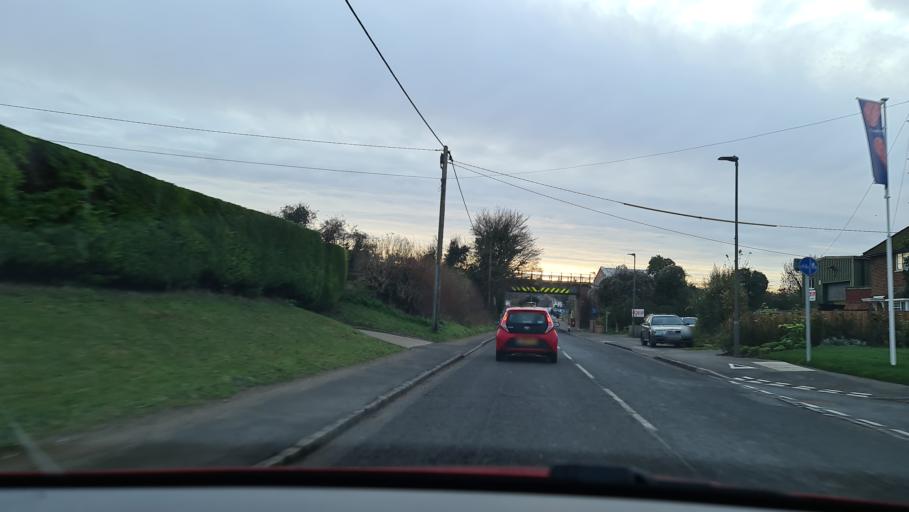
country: GB
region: England
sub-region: Buckinghamshire
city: Princes Risborough
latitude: 51.7296
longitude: -0.8362
